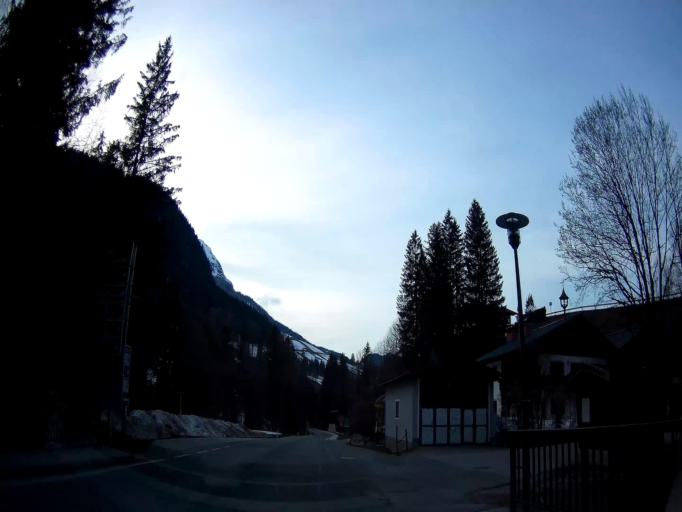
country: AT
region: Salzburg
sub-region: Politischer Bezirk Hallein
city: Abtenau
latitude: 47.5256
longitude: 13.4289
